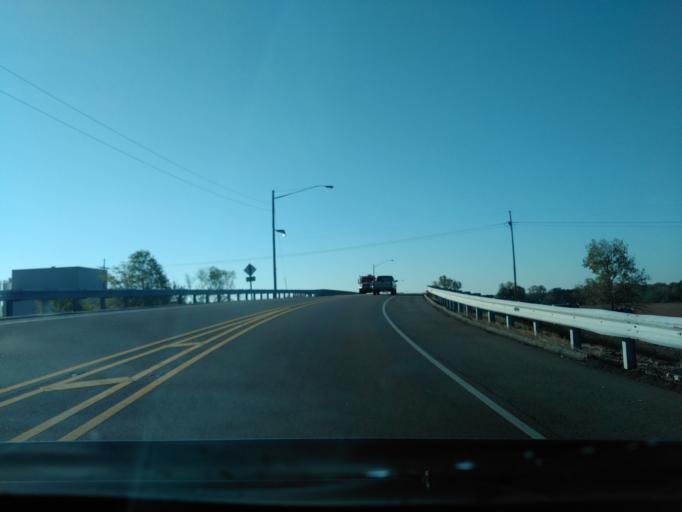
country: US
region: Illinois
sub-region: Bond County
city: Greenville
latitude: 38.8855
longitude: -89.3909
